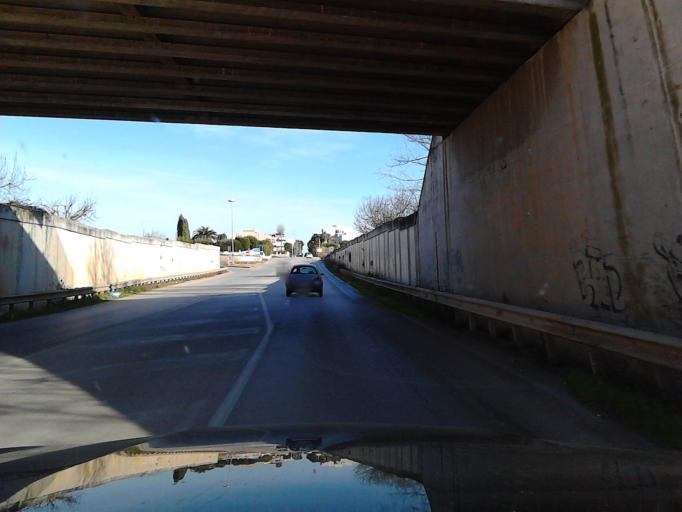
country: IT
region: Apulia
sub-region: Provincia di Bari
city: Rutigliano
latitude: 41.0073
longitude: 16.9914
